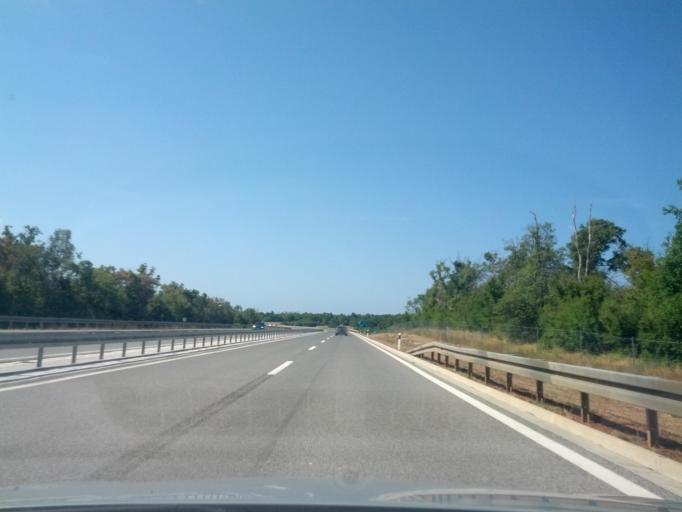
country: HR
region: Istarska
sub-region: Grad Rovinj
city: Rovinj
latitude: 45.1665
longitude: 13.7303
